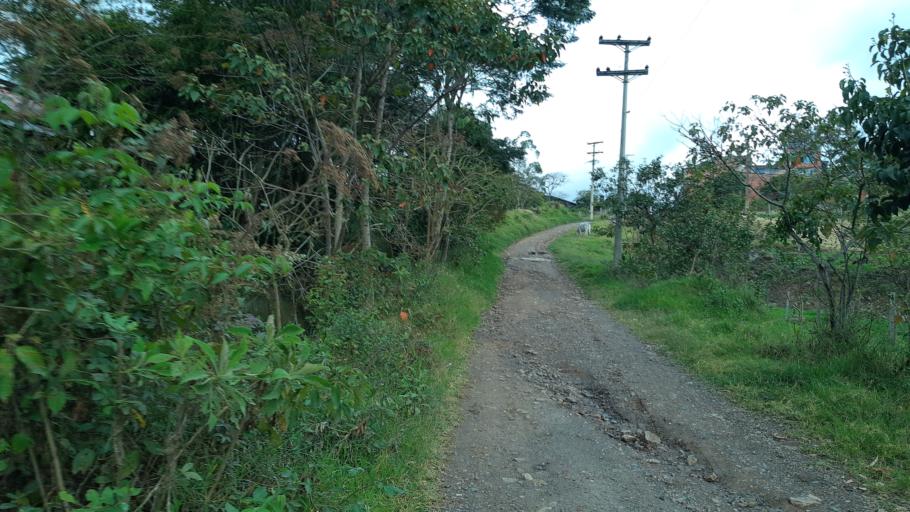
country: CO
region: Boyaca
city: Garagoa
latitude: 5.0845
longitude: -73.3688
